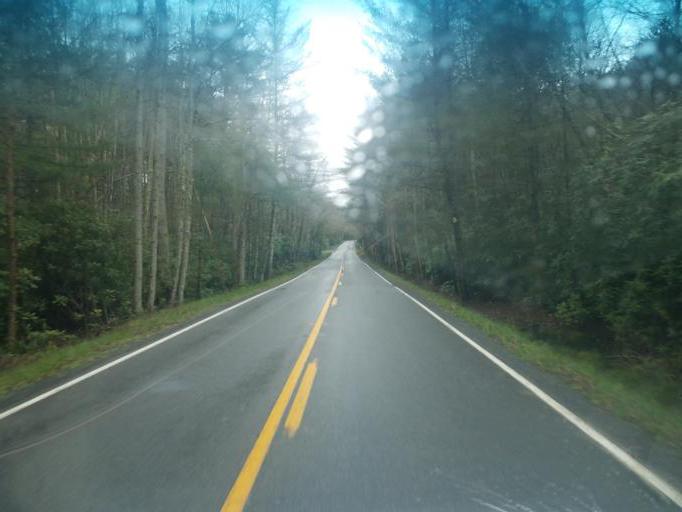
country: US
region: Virginia
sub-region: Smyth County
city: Chilhowie
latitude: 36.6536
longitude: -81.6950
